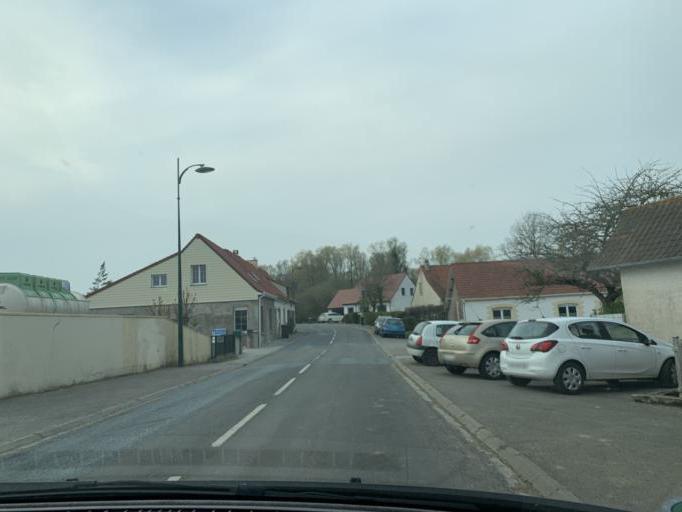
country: FR
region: Nord-Pas-de-Calais
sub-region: Departement du Pas-de-Calais
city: Longfosse
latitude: 50.6996
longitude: 1.7853
